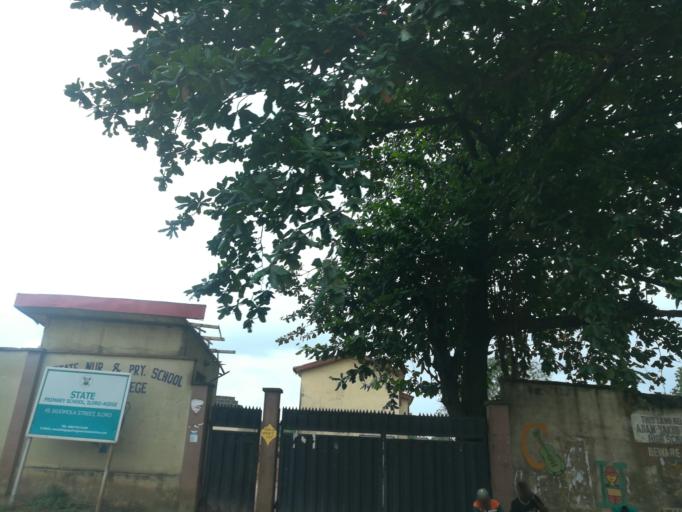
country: NG
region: Lagos
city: Agege
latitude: 6.6090
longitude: 3.3230
